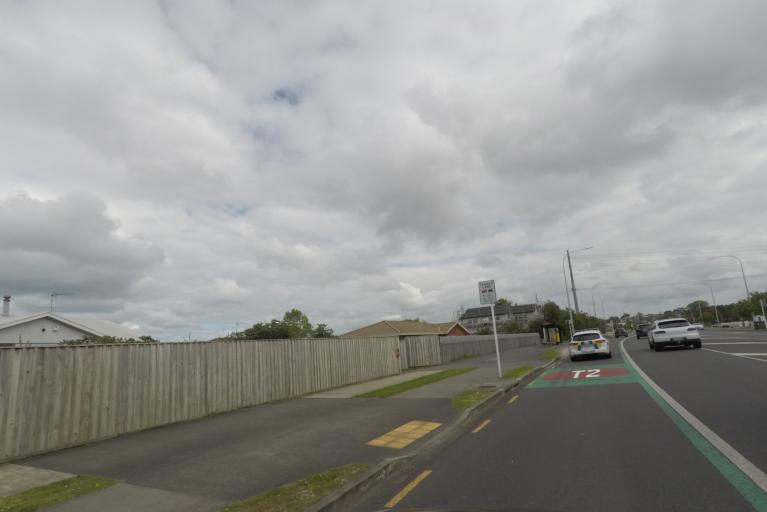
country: NZ
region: Auckland
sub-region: Auckland
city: Rothesay Bay
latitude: -36.7383
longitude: 174.6923
